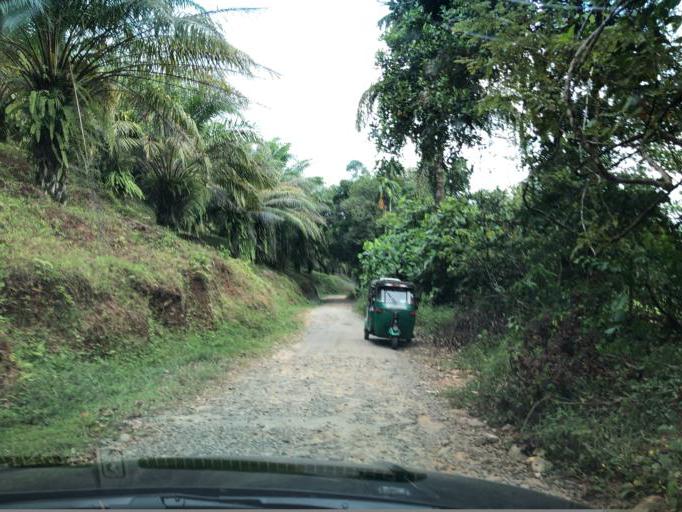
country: LK
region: Western
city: Horawala Junction
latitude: 6.5462
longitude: 80.0942
